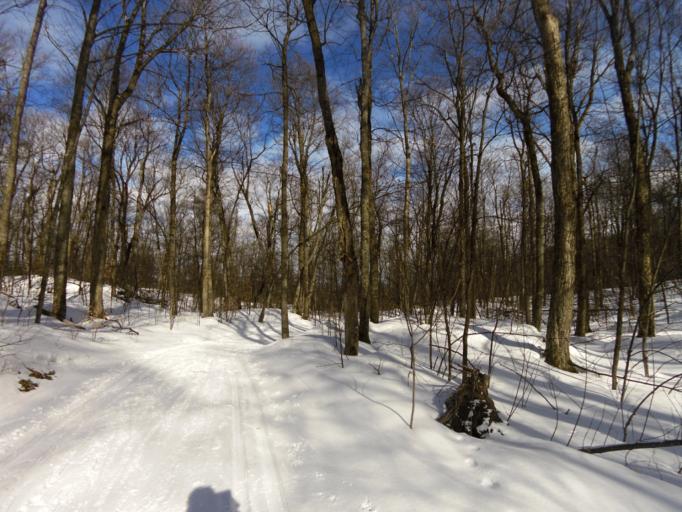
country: CA
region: Quebec
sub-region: Outaouais
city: Wakefield
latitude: 45.5280
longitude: -75.9045
